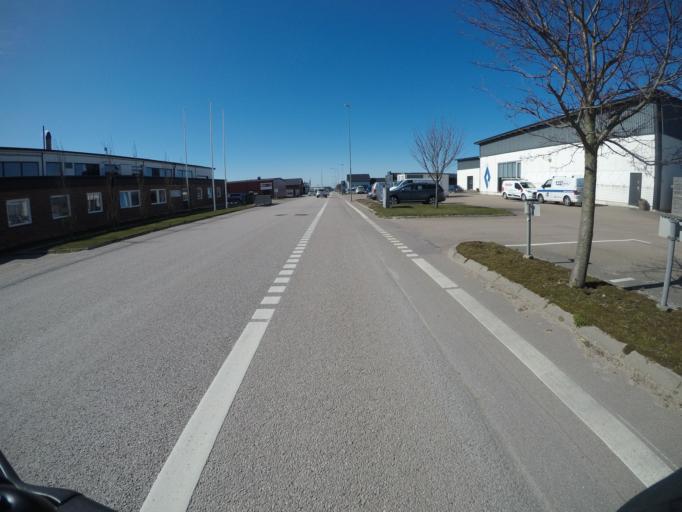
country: SE
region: Halland
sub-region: Laholms Kommun
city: Laholm
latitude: 56.5006
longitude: 13.0225
